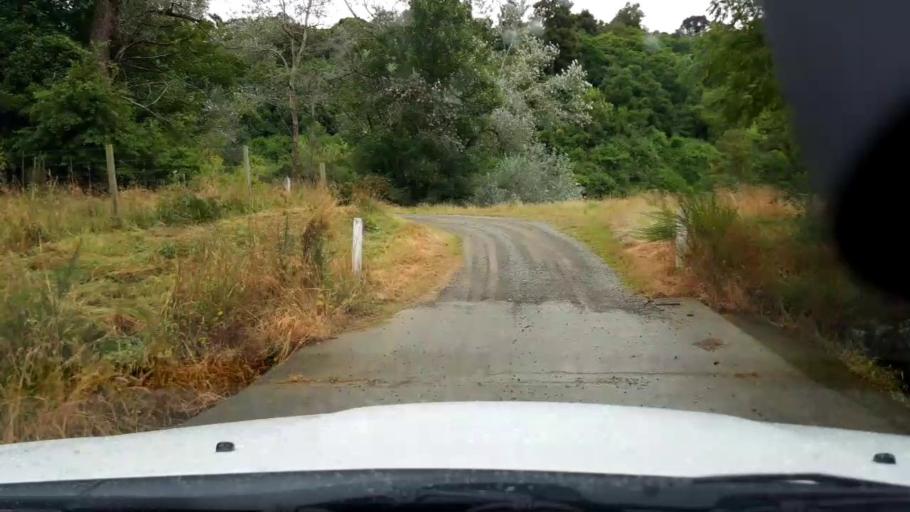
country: NZ
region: Canterbury
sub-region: Timaru District
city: Pleasant Point
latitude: -44.1088
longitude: 171.1359
